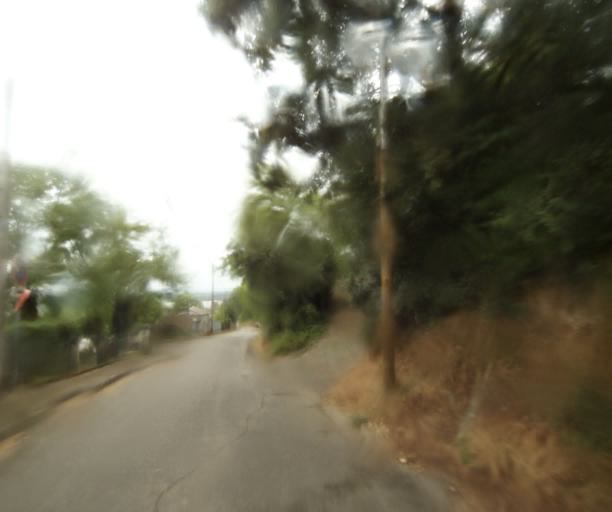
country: FR
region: Rhone-Alpes
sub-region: Departement de l'Ain
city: Miribel
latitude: 45.8269
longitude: 4.9491
